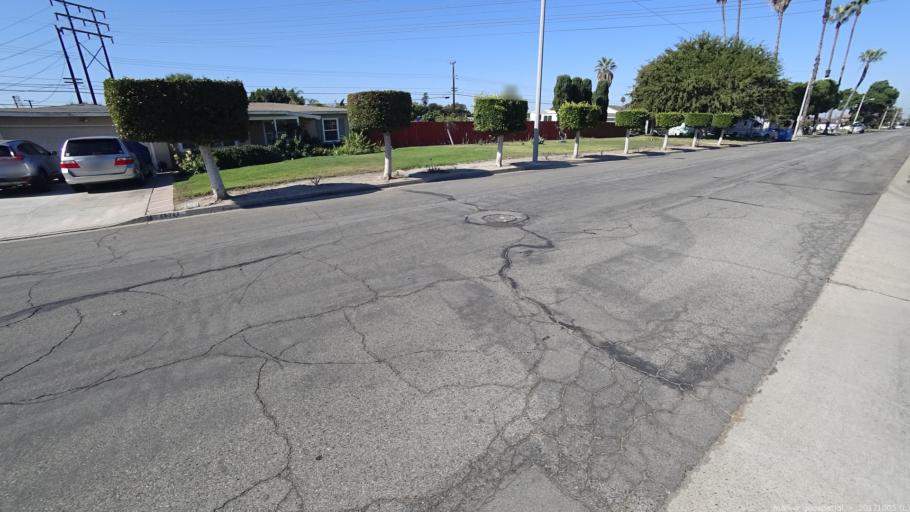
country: US
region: California
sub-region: Orange County
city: Stanton
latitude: 33.7981
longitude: -117.9794
